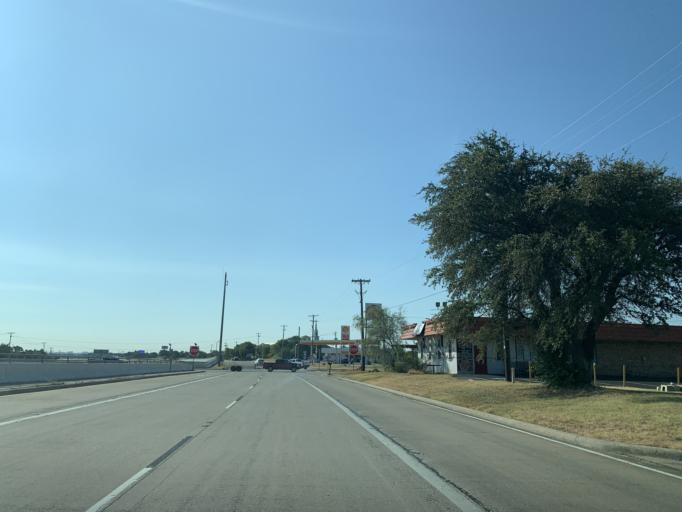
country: US
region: Texas
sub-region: Tarrant County
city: Lakeside
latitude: 32.8269
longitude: -97.4808
